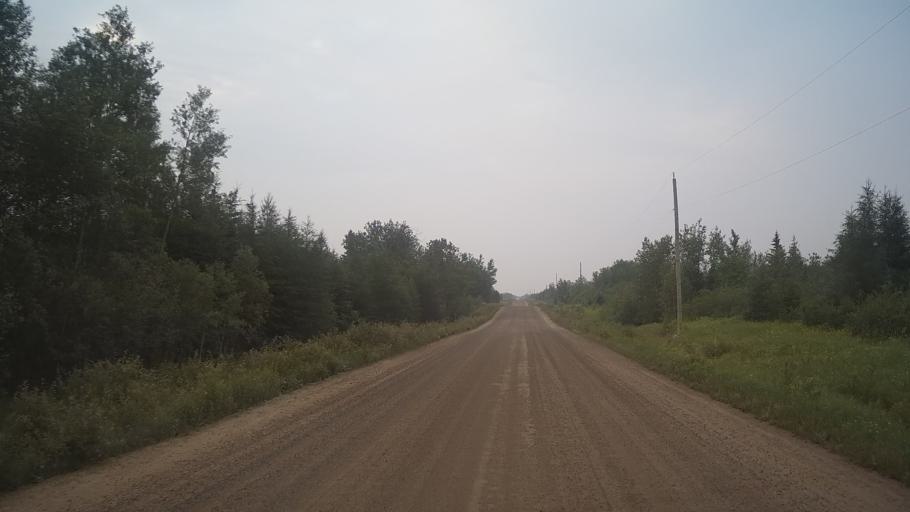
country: CA
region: Ontario
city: Hearst
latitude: 49.6361
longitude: -83.2783
